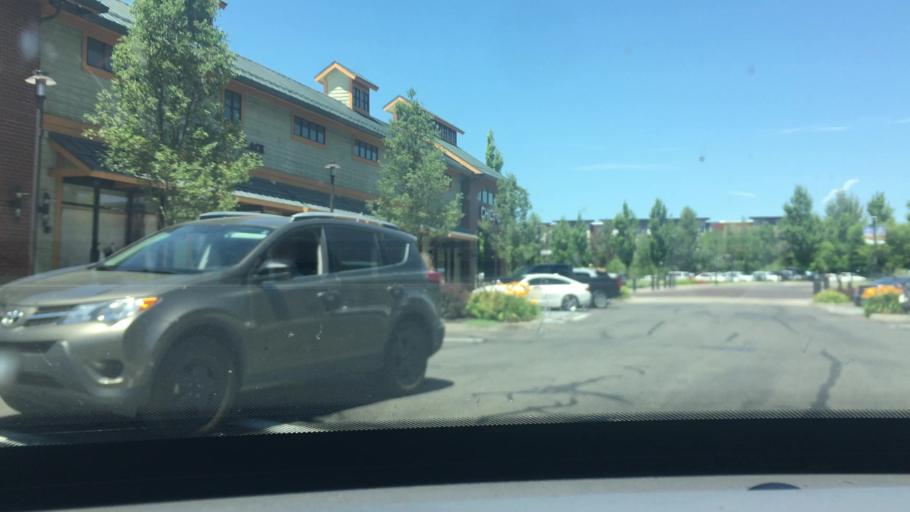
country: US
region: Oregon
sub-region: Deschutes County
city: Bend
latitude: 44.0470
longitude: -121.3148
